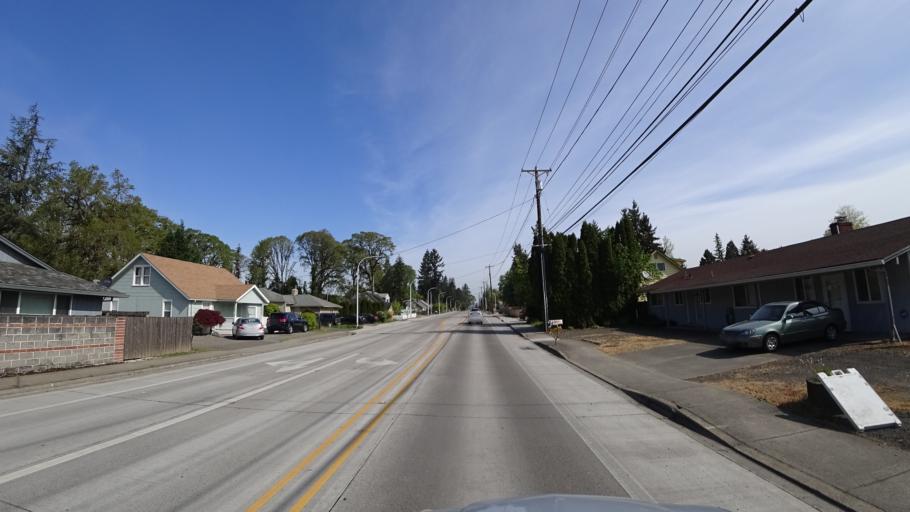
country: US
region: Oregon
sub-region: Washington County
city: Hillsboro
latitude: 45.5213
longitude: -122.9545
